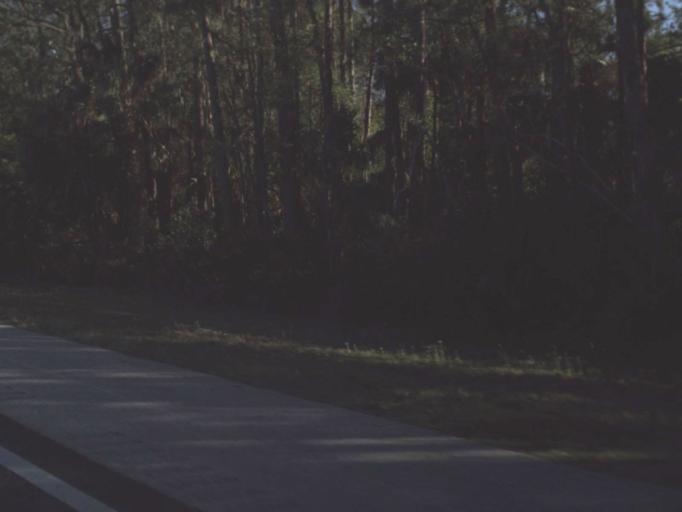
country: US
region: Florida
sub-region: Flagler County
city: Palm Coast
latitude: 29.6327
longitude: -81.2662
